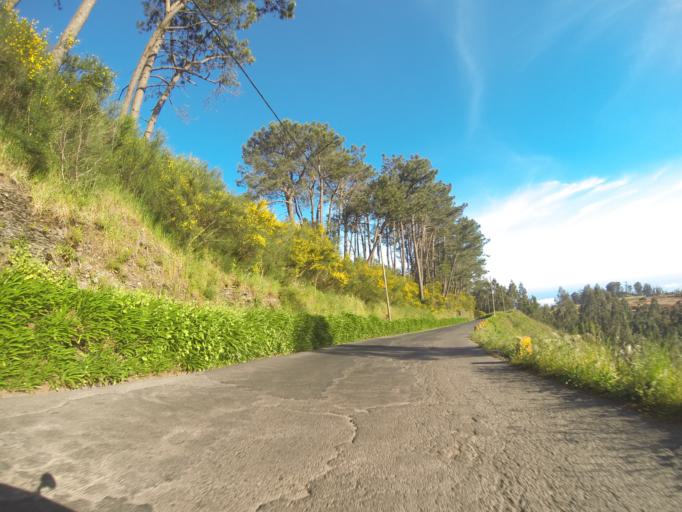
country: PT
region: Madeira
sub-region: Santa Cruz
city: Camacha
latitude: 32.6904
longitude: -16.8759
